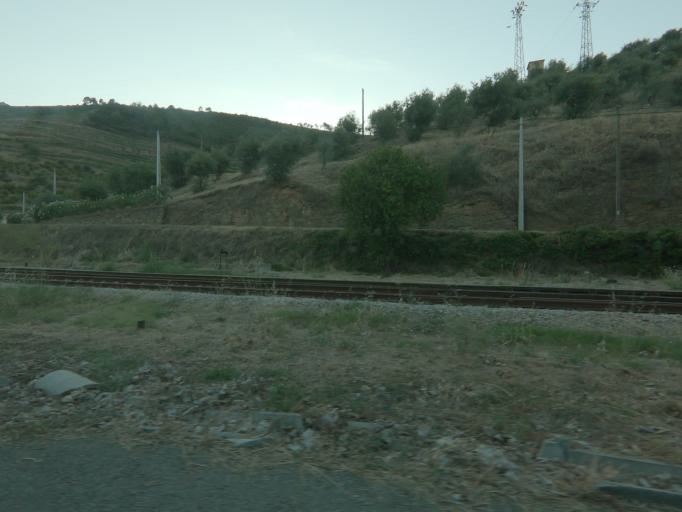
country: PT
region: Viseu
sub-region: Armamar
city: Armamar
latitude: 41.1536
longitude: -7.6865
